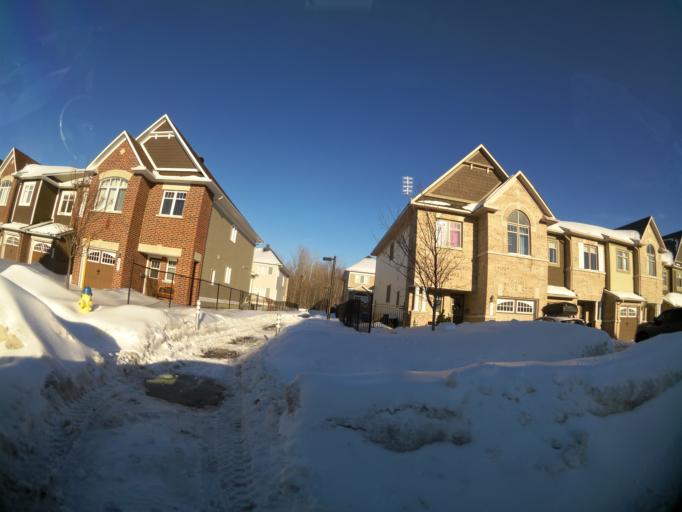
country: CA
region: Ontario
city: Ottawa
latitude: 45.4330
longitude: -75.5152
